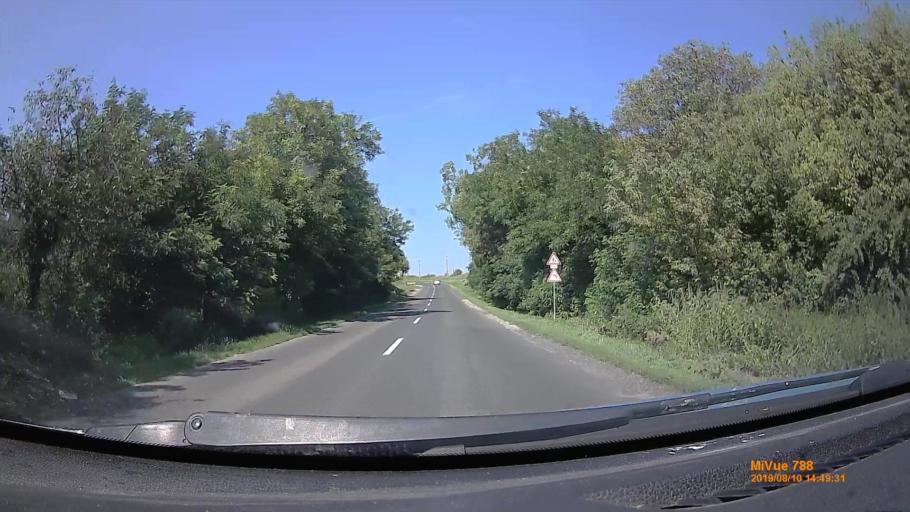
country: HU
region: Somogy
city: Somogyvar
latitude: 46.5981
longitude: 17.6443
